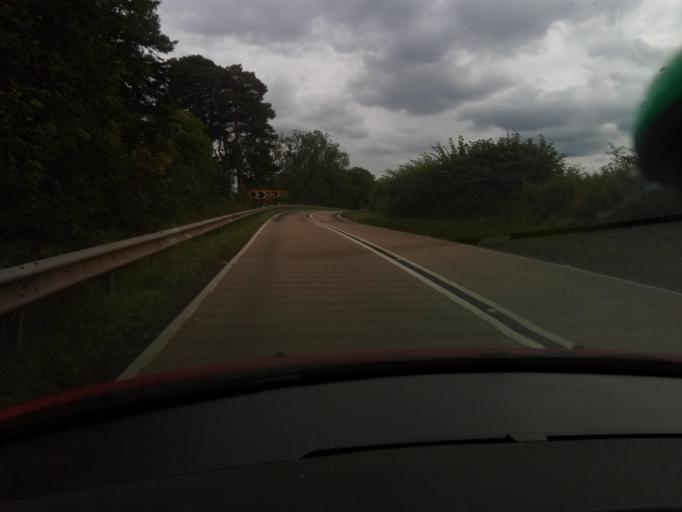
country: GB
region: Scotland
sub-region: The Scottish Borders
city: Jedburgh
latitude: 55.4014
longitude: -2.5008
